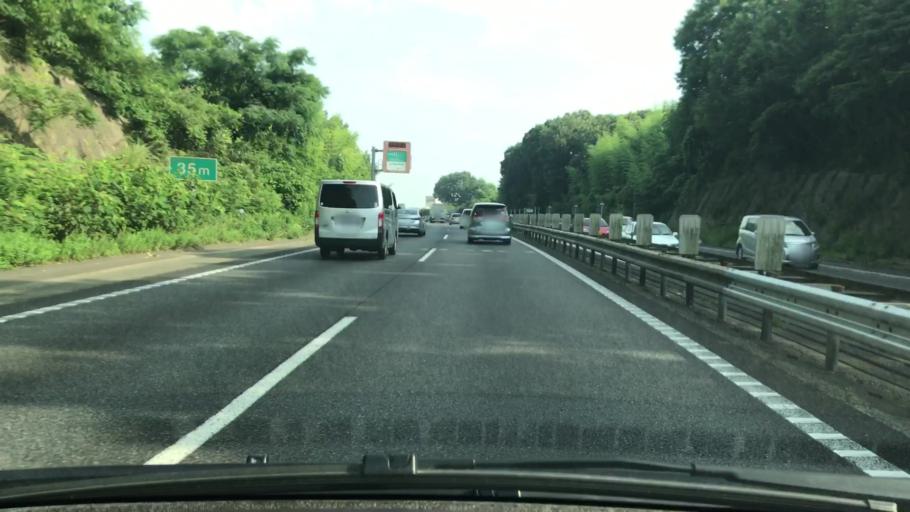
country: JP
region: Hyogo
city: Akashi
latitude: 34.6950
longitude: 134.9686
